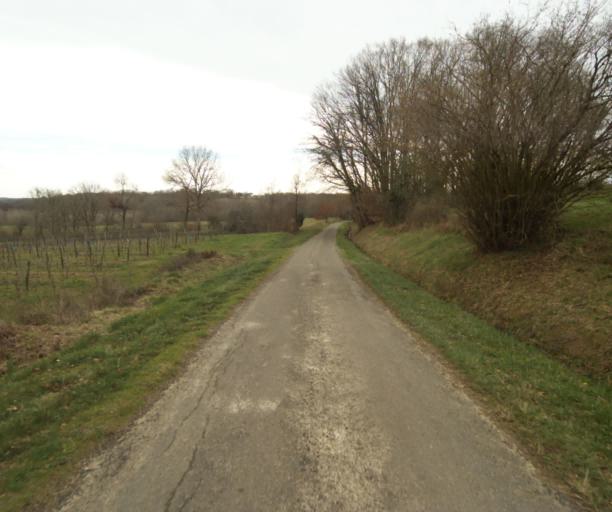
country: FR
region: Midi-Pyrenees
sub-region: Departement du Gers
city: Eauze
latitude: 43.9080
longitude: 0.0613
